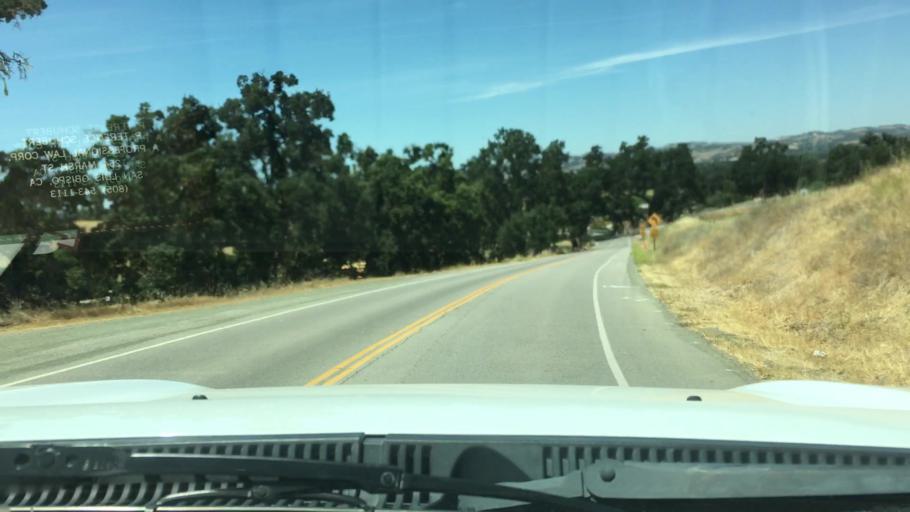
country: US
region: California
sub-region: San Luis Obispo County
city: Templeton
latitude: 35.5575
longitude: -120.6852
